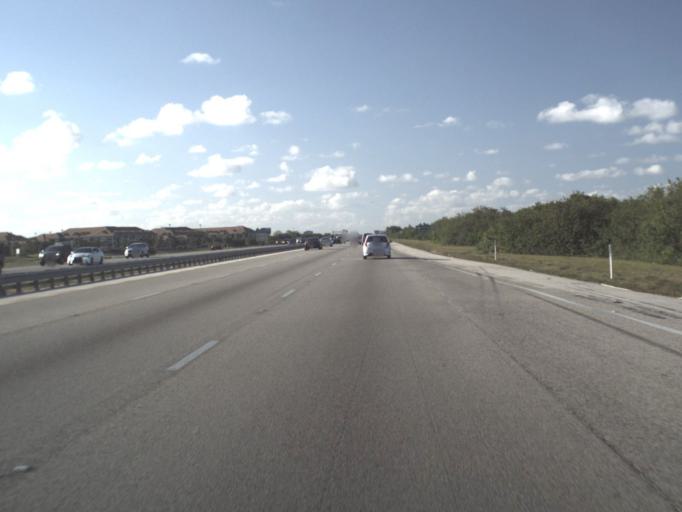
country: US
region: Florida
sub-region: Brevard County
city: Rockledge
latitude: 28.2411
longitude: -80.7215
